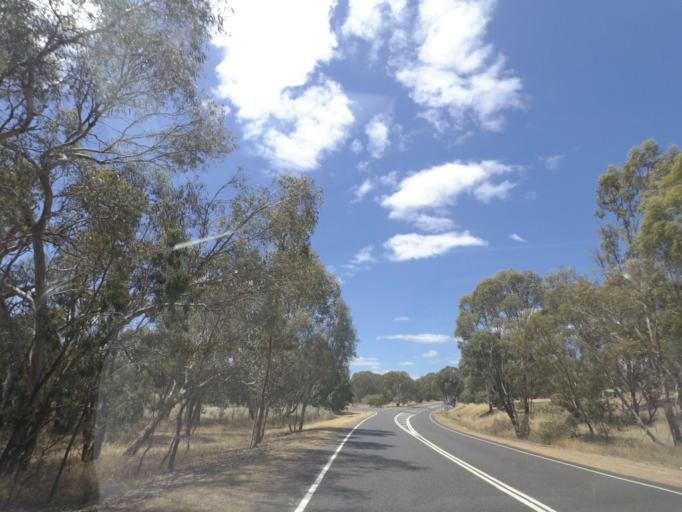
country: AU
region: Victoria
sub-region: Wangaratta
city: Wangaratta
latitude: -36.4647
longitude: 146.2154
